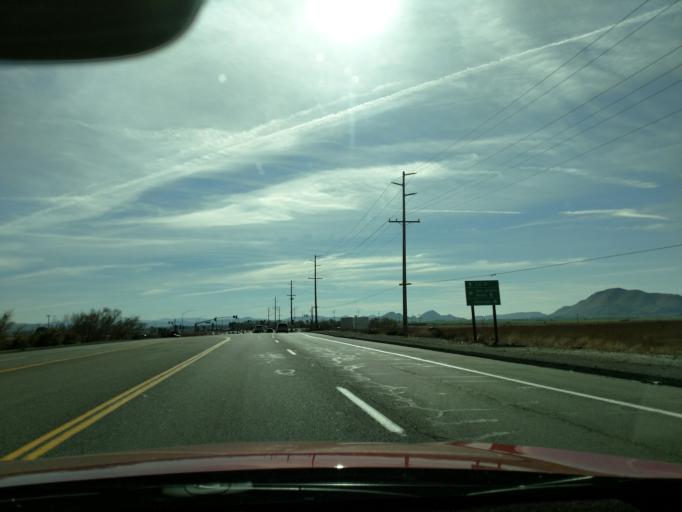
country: US
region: California
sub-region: Riverside County
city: San Jacinto
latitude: 33.8258
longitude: -117.0036
